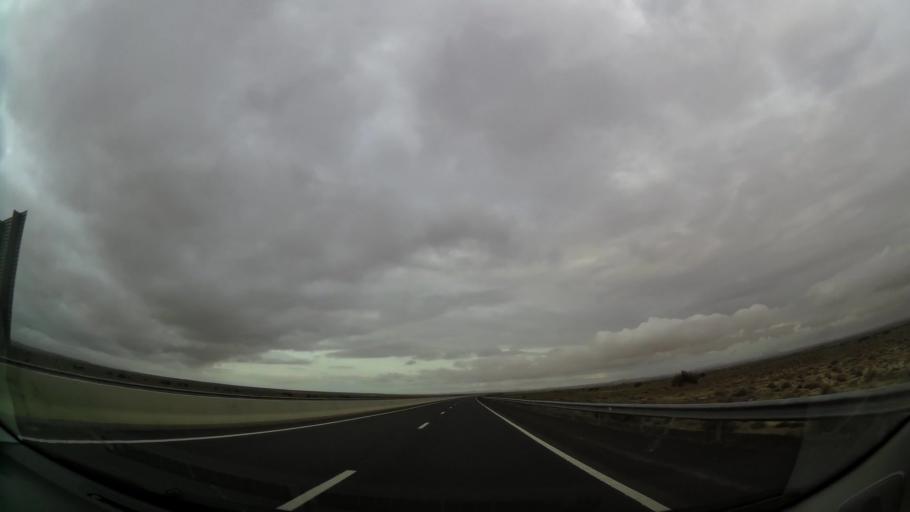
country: MA
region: Taza-Al Hoceima-Taounate
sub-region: Taza
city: Guercif
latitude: 34.3737
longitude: -3.2623
